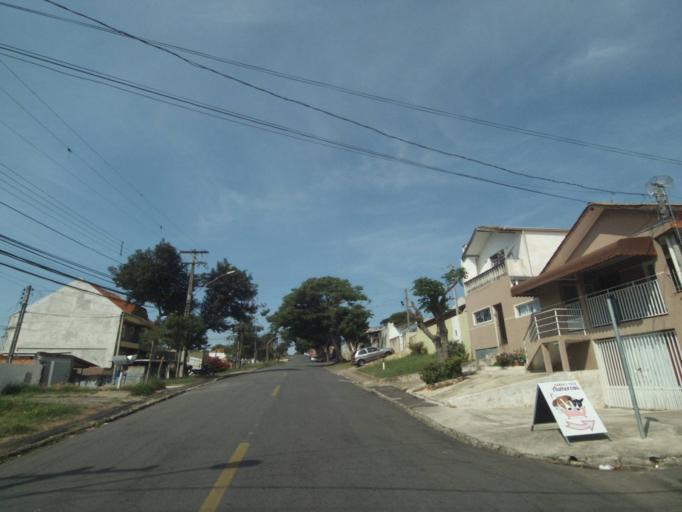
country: BR
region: Parana
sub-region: Curitiba
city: Curitiba
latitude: -25.4640
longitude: -49.3161
